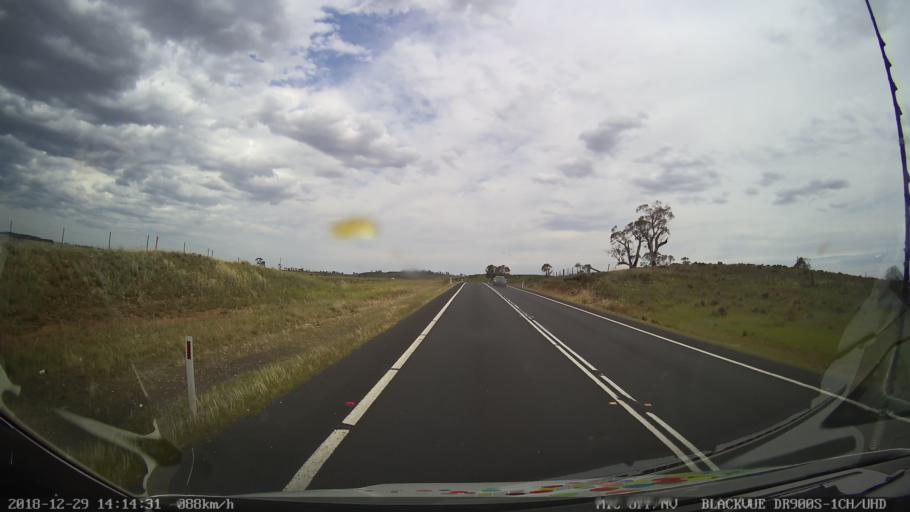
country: AU
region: New South Wales
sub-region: Cooma-Monaro
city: Cooma
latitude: -36.4435
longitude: 149.2373
